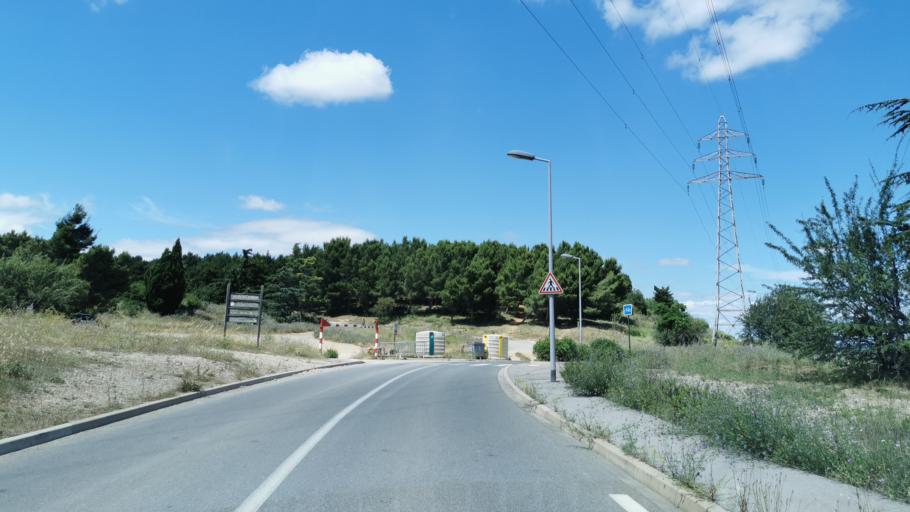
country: FR
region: Languedoc-Roussillon
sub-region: Departement de l'Aude
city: Narbonne
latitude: 43.1874
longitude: 2.9722
